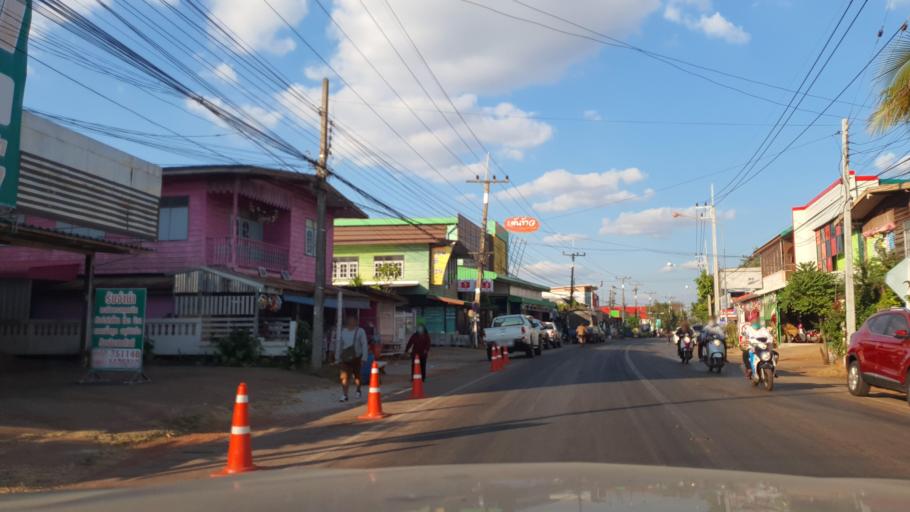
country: TH
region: Sakon Nakhon
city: Sakon Nakhon
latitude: 17.2571
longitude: 104.1882
